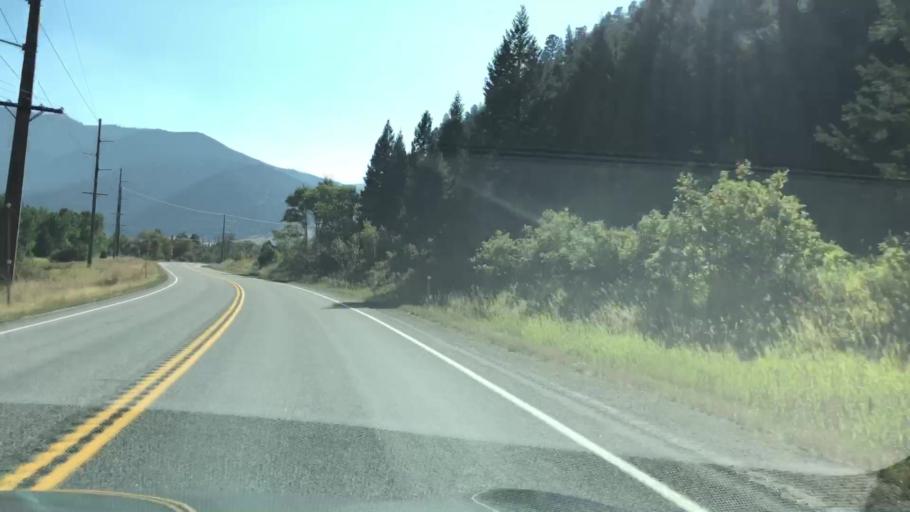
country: US
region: Montana
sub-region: Gallatin County
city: Four Corners
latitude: 45.5048
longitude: -111.2668
